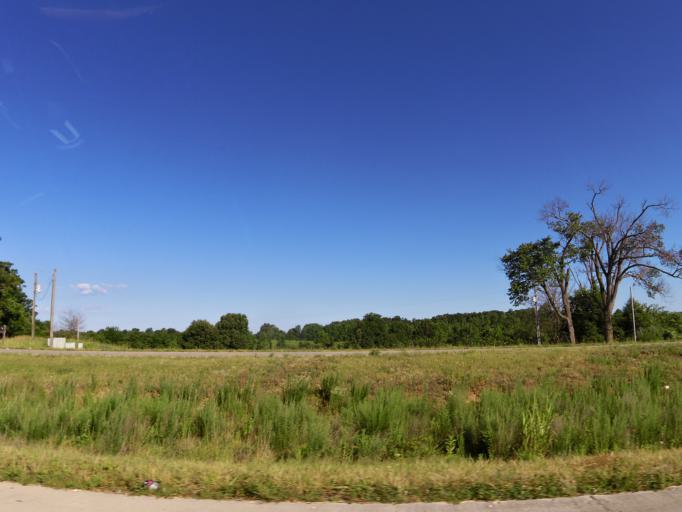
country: US
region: Missouri
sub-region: Butler County
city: Poplar Bluff
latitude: 36.6866
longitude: -90.4856
